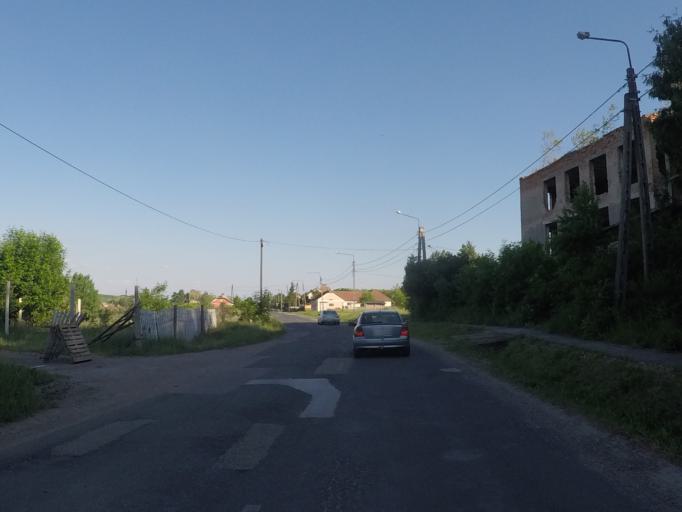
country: HU
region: Borsod-Abauj-Zemplen
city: Sajokaza
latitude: 48.3204
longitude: 20.6140
